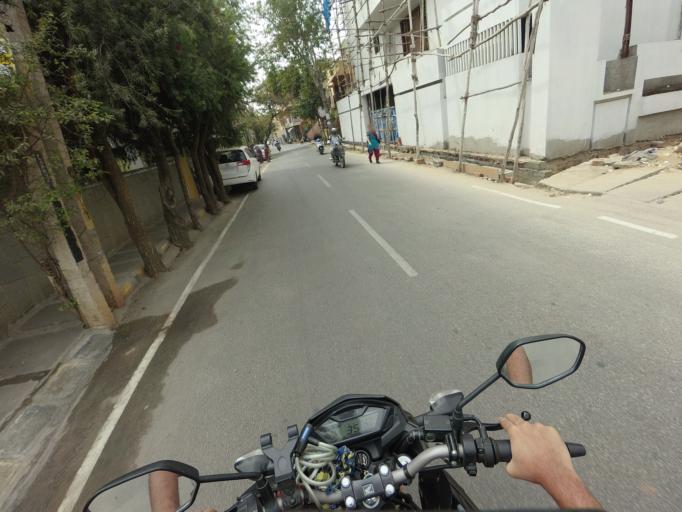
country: IN
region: Karnataka
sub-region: Bangalore Urban
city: Bangalore
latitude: 12.9729
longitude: 77.5321
